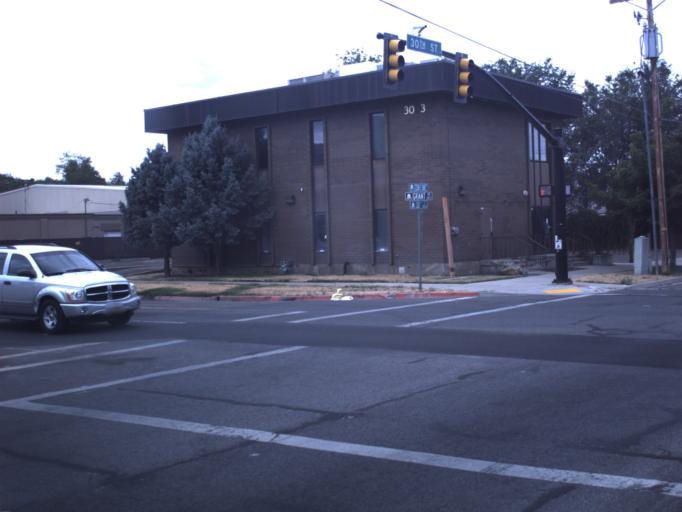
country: US
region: Utah
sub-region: Weber County
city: Ogden
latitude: 41.2103
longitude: -111.9734
